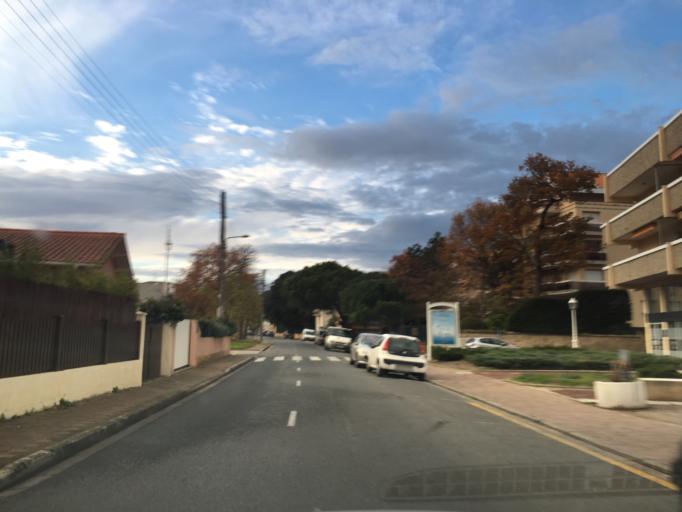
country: FR
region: Aquitaine
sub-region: Departement de la Gironde
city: Arcachon
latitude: 44.6623
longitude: -1.1590
